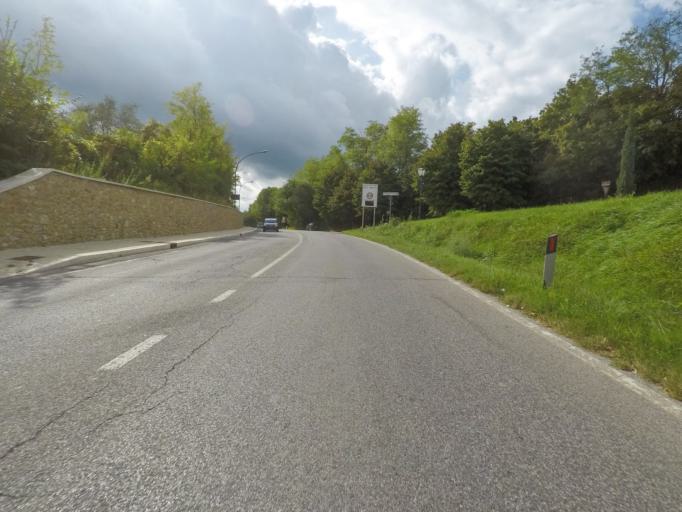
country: IT
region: Tuscany
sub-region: Provincia di Siena
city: Montepulciano
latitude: 43.1074
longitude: 11.7863
